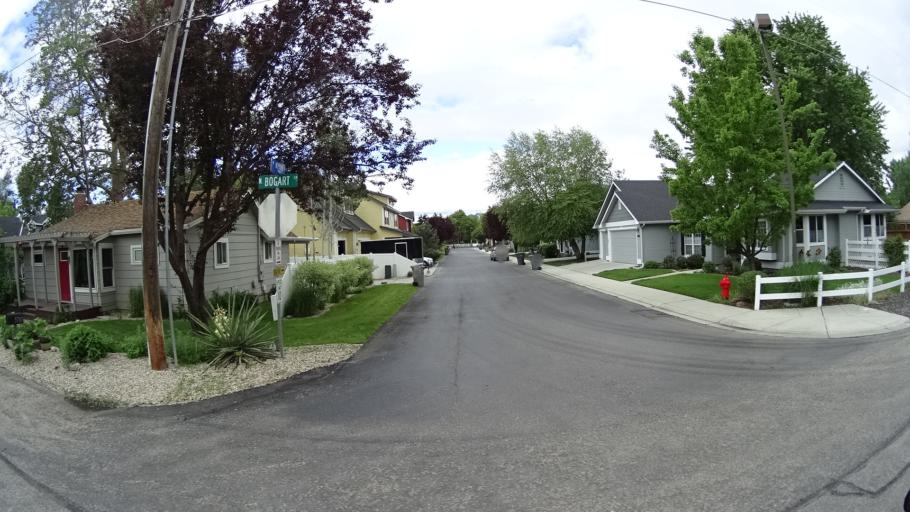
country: US
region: Idaho
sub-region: Ada County
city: Eagle
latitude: 43.6719
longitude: -116.2943
